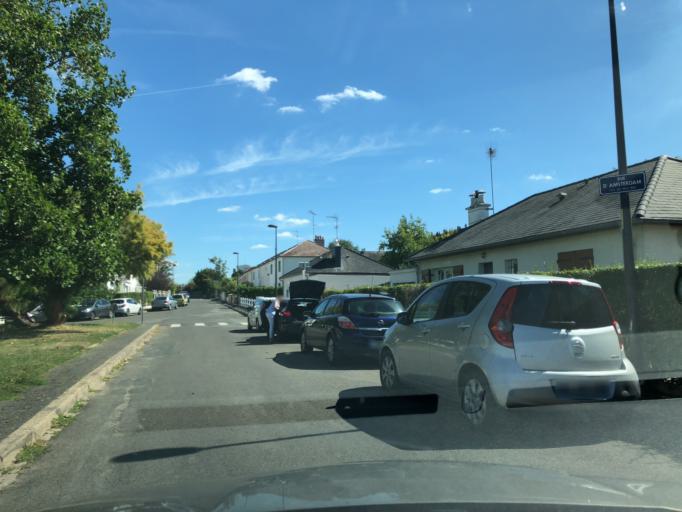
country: FR
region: Centre
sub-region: Departement d'Indre-et-Loire
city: Saint-Cyr-sur-Loire
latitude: 47.4238
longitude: 0.6855
